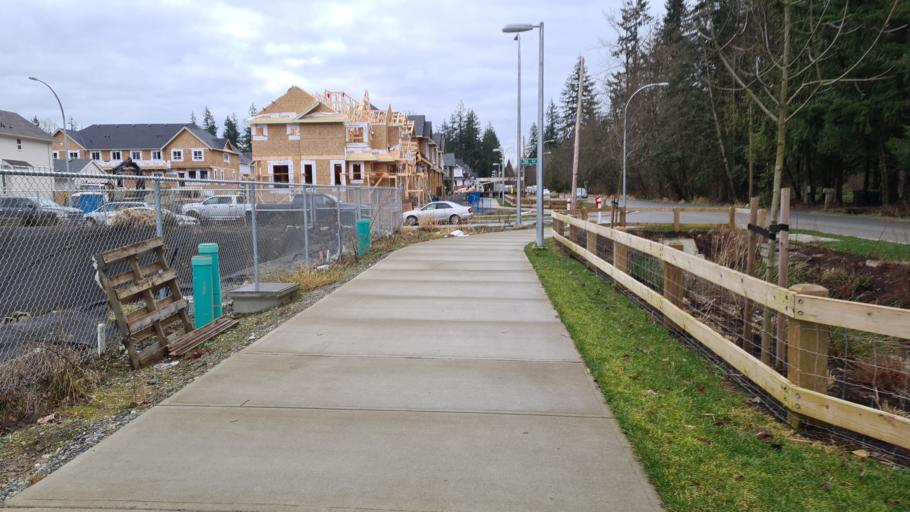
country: CA
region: British Columbia
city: Walnut Grove
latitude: 49.1456
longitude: -122.6568
